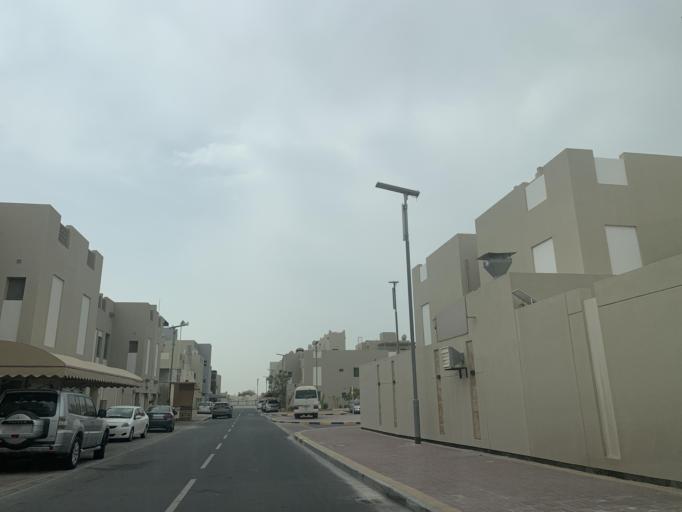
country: BH
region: Northern
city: Madinat `Isa
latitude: 26.1691
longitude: 50.5109
